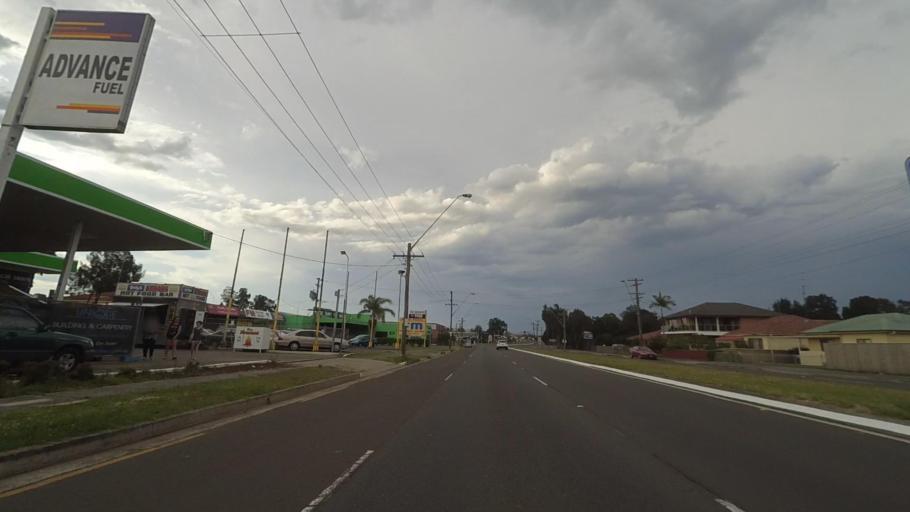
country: AU
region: New South Wales
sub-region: Shellharbour
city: Barrack Heights
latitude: -34.5595
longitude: 150.8597
